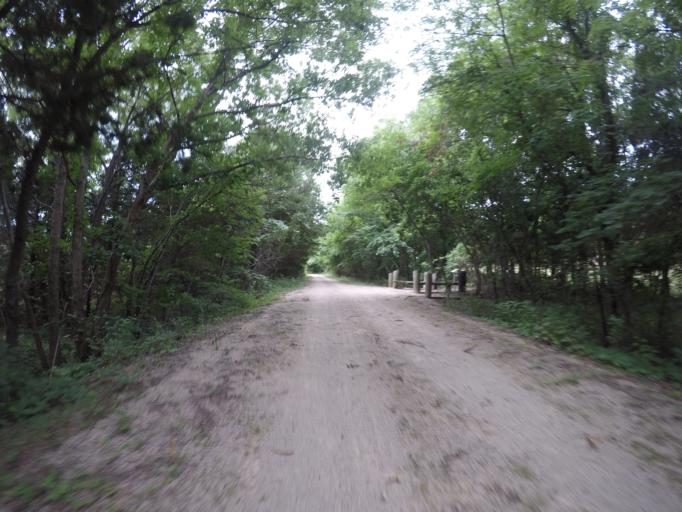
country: US
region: Kansas
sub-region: Anderson County
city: Garnett
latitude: 38.3299
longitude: -95.2470
